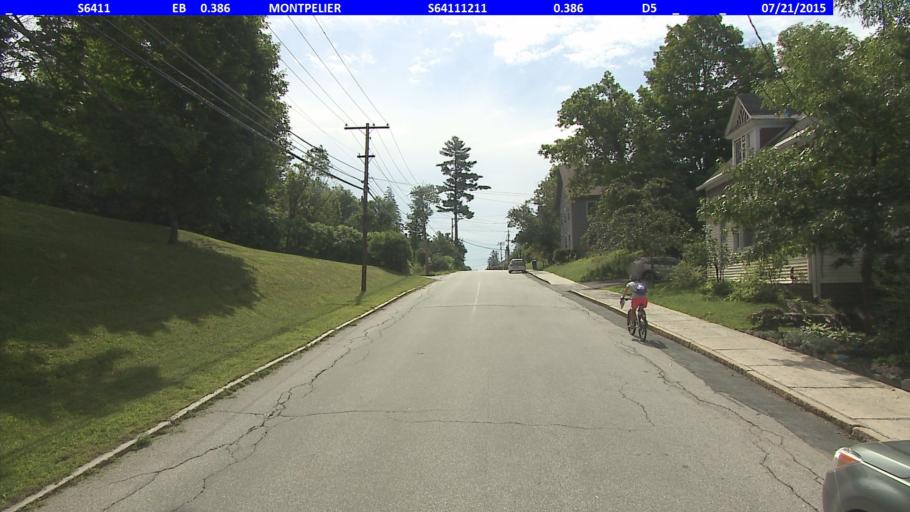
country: US
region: Vermont
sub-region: Washington County
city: Montpelier
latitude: 44.2572
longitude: -72.5688
